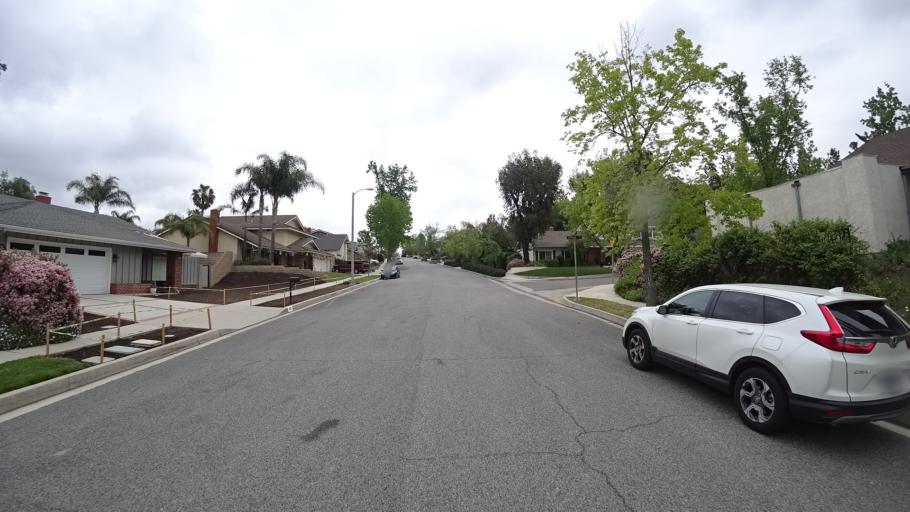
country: US
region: California
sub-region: Ventura County
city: Thousand Oaks
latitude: 34.2019
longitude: -118.8868
